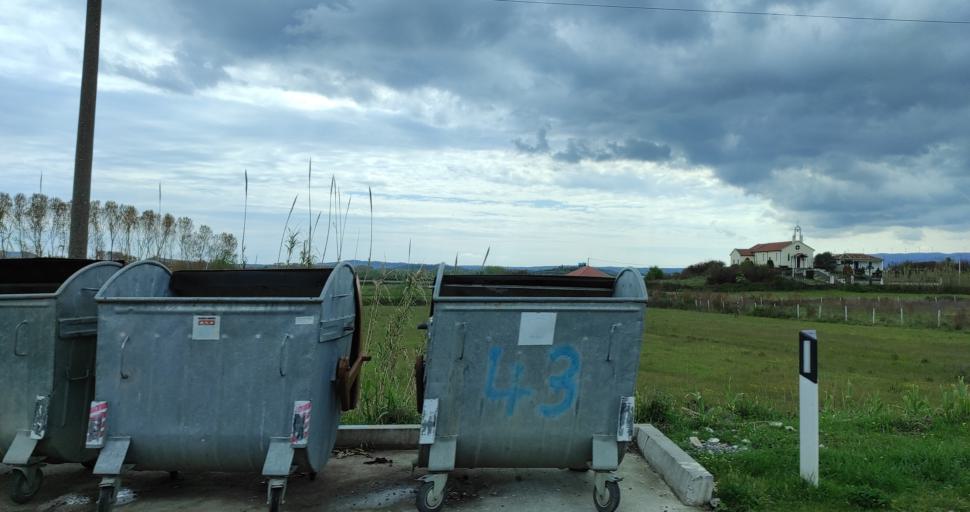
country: AL
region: Shkoder
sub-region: Rrethi i Shkodres
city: Dajc
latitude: 42.0155
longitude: 19.4001
